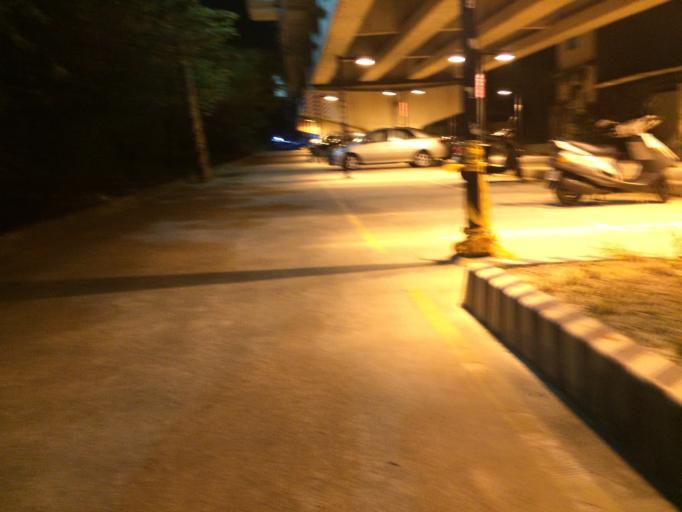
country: TW
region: Taiwan
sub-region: Hsinchu
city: Zhubei
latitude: 24.7868
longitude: 121.0225
